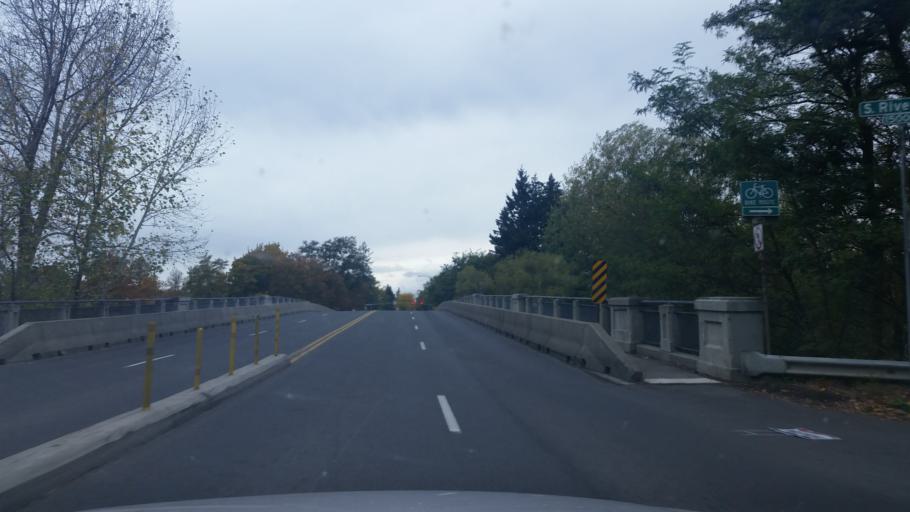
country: US
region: Washington
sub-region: Spokane County
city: Spokane
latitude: 47.6718
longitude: -117.3866
